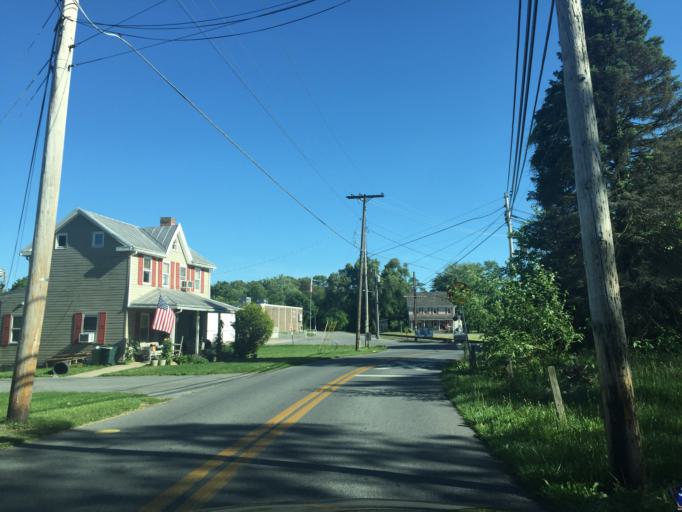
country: US
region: Maryland
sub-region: Baltimore County
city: Reisterstown
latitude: 39.5314
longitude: -76.8227
